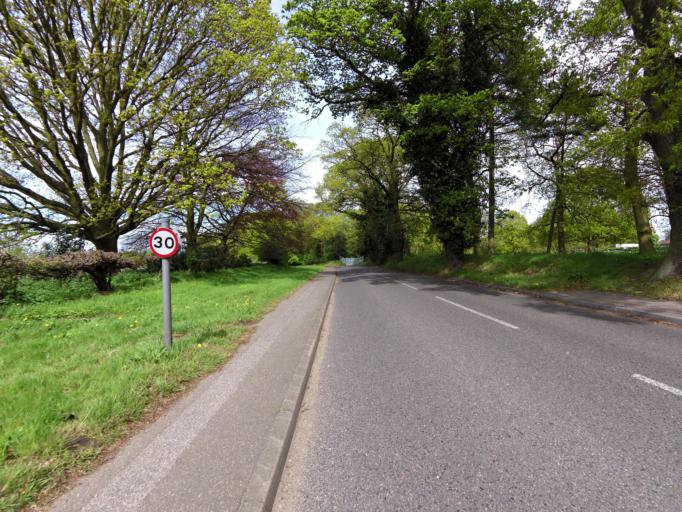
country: GB
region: England
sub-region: Essex
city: Mistley
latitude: 51.9749
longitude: 1.1521
